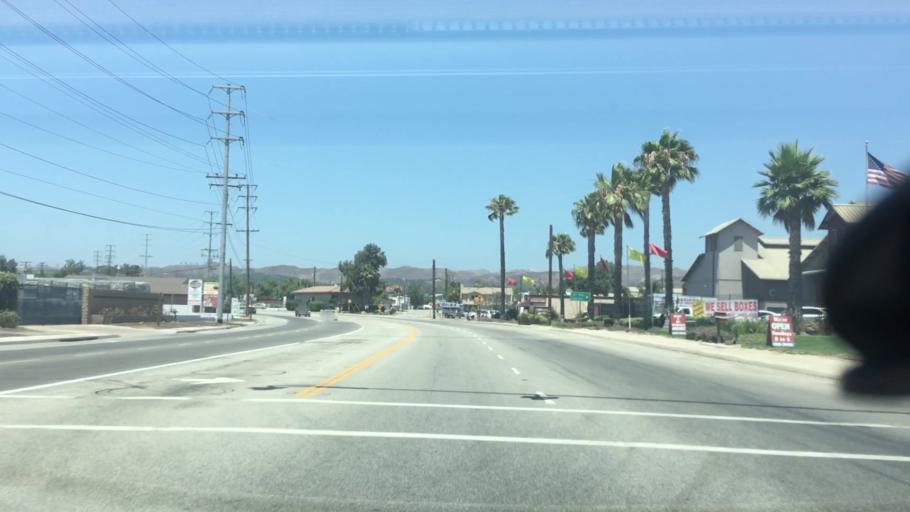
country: US
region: California
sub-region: Ventura County
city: Saticoy
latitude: 34.2810
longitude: -119.1448
